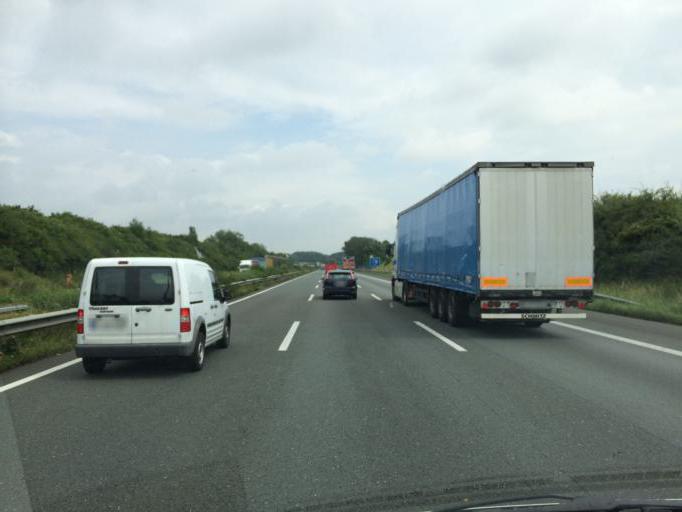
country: DE
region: North Rhine-Westphalia
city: Porta Westfalica
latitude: 52.2095
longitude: 8.9140
